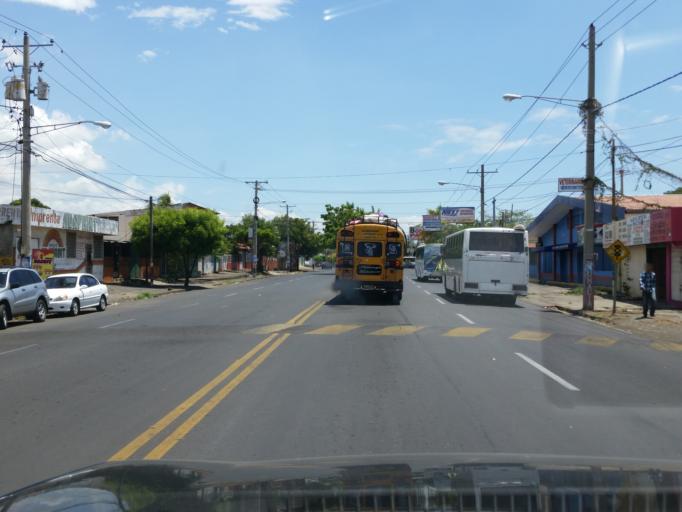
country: NI
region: Managua
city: Managua
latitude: 12.1457
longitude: -86.2493
